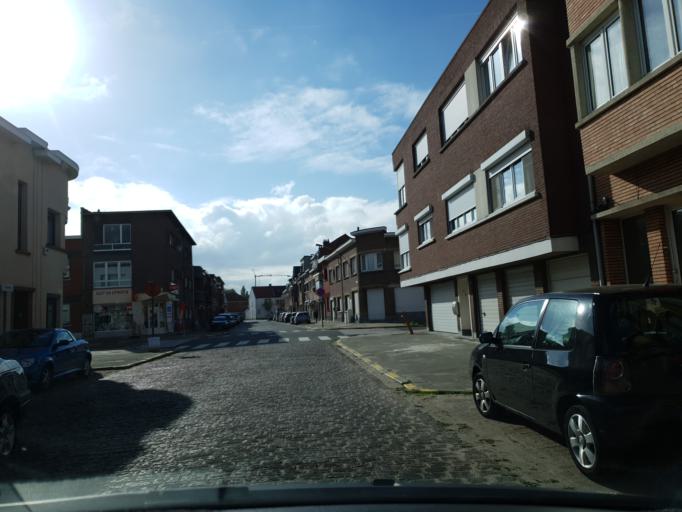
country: BE
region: Flanders
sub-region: Provincie Antwerpen
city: Schoten
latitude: 51.2537
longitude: 4.4531
